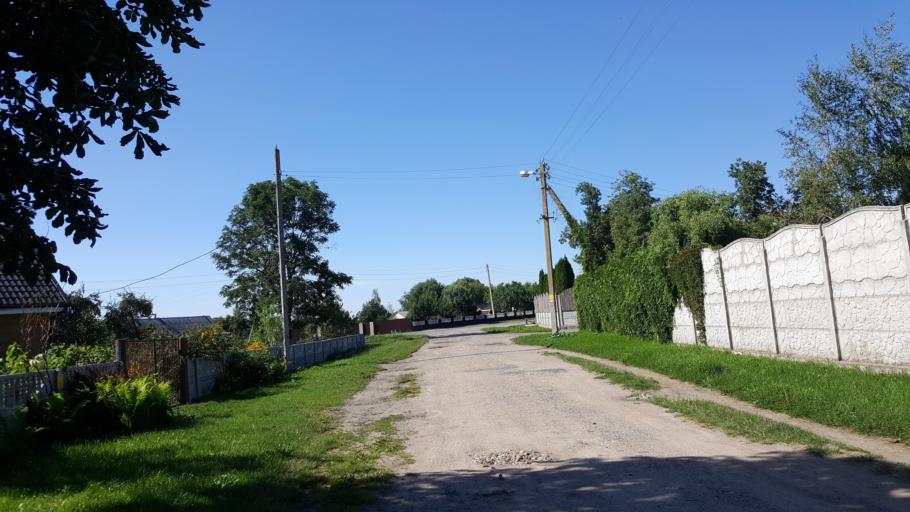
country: BY
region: Brest
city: Charnawchytsy
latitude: 52.2108
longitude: 23.7385
